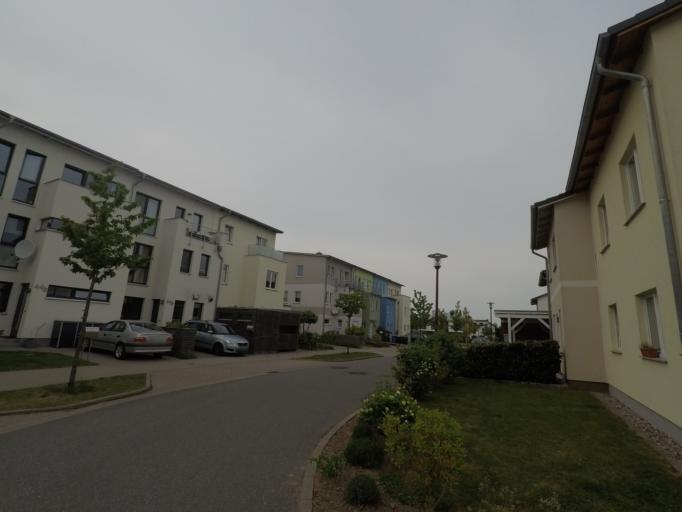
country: DE
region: Mecklenburg-Vorpommern
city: Rostock
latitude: 54.0674
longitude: 12.1257
